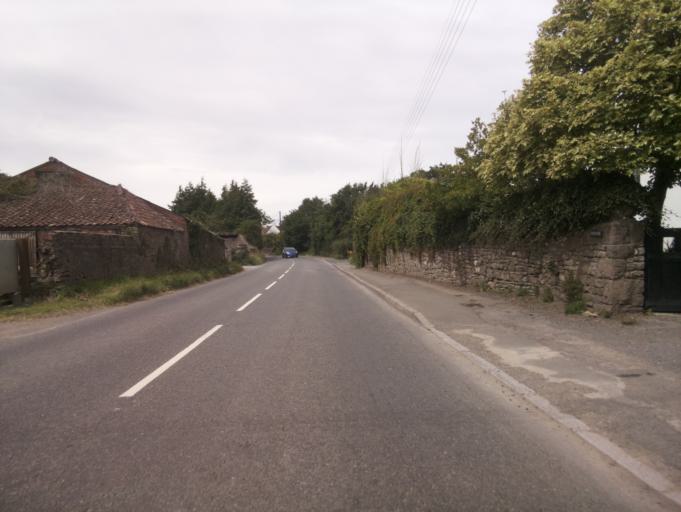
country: GB
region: England
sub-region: North Somerset
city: Yatton
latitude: 51.3996
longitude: -2.8377
